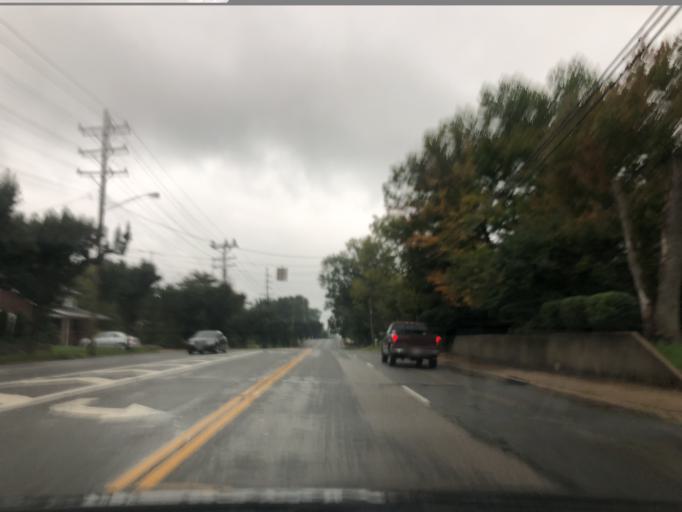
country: US
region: Ohio
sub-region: Hamilton County
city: Blue Ash
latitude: 39.2245
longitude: -84.3778
